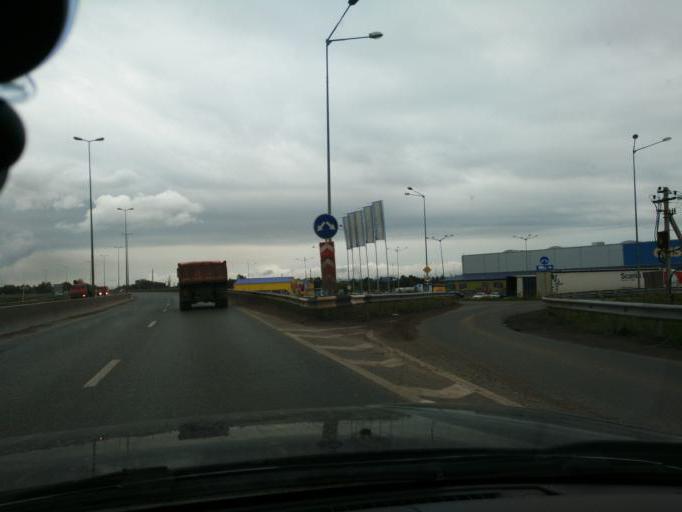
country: RU
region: Perm
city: Kondratovo
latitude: 57.9500
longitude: 56.1224
